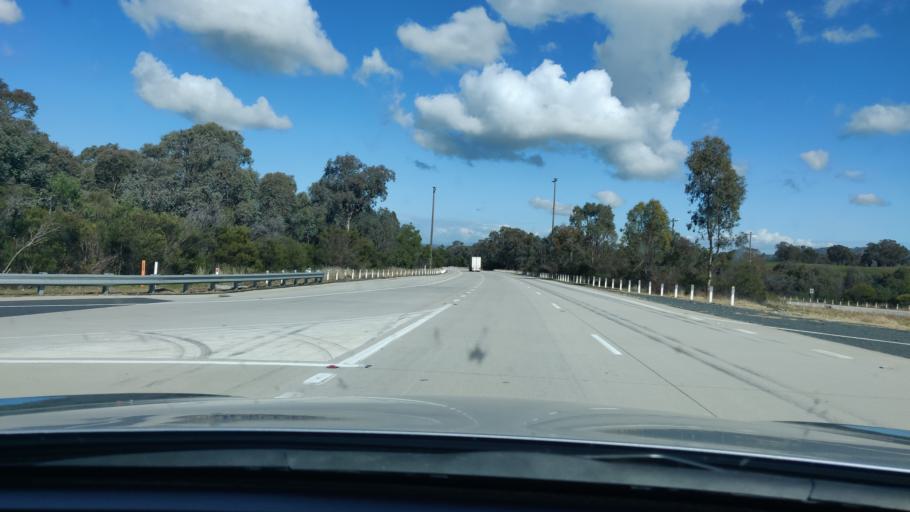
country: AU
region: New South Wales
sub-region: Greater Hume Shire
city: Holbrook
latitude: -35.8454
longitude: 147.1957
